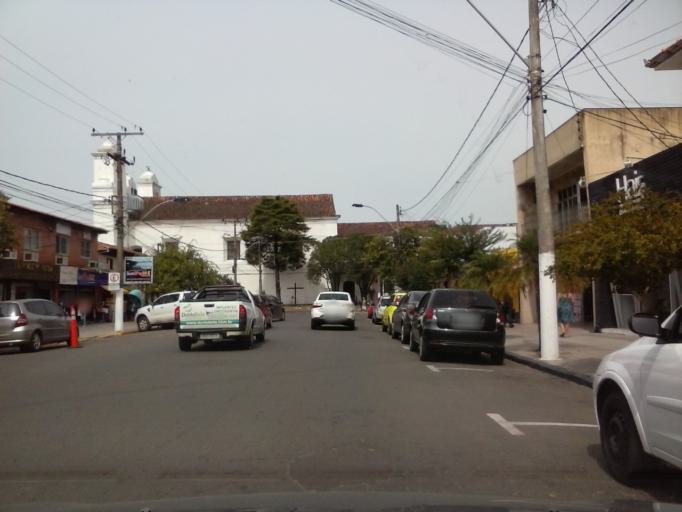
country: BR
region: Rio Grande do Sul
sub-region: Viamao
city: Viamao
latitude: -30.0824
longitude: -51.0250
